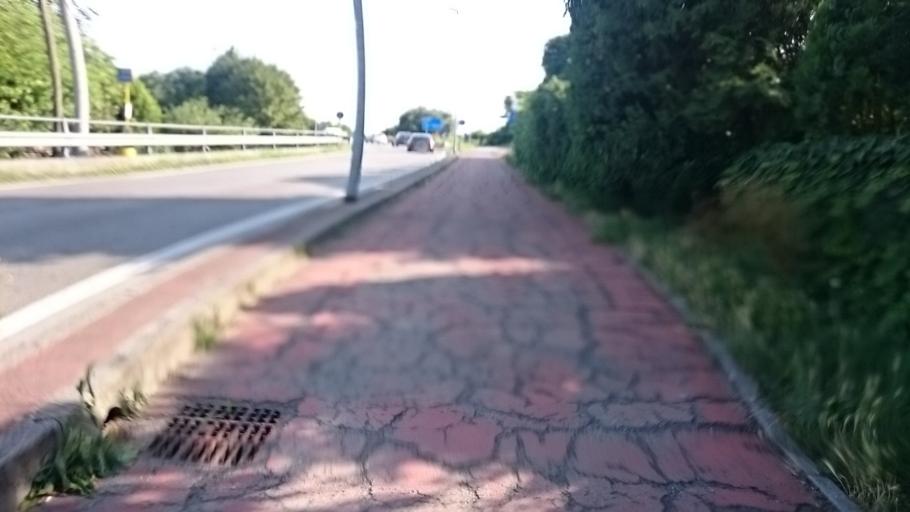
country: IT
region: Veneto
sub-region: Provincia di Venezia
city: Galta
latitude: 45.3879
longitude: 12.0174
